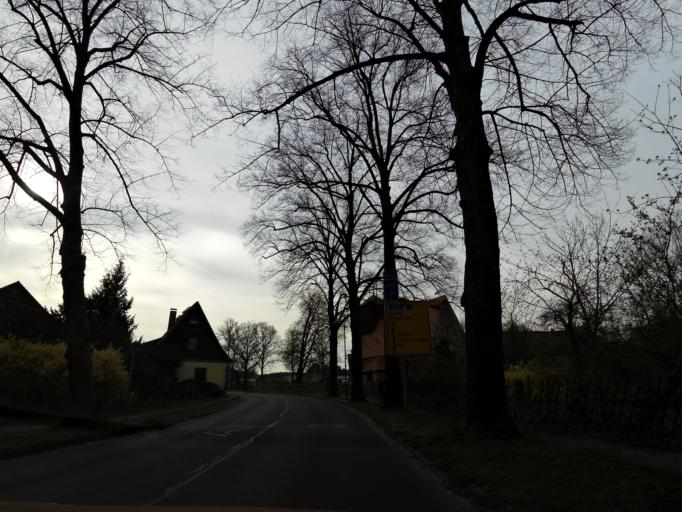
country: DE
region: Brandenburg
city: Bestensee
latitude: 52.2433
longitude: 13.6286
